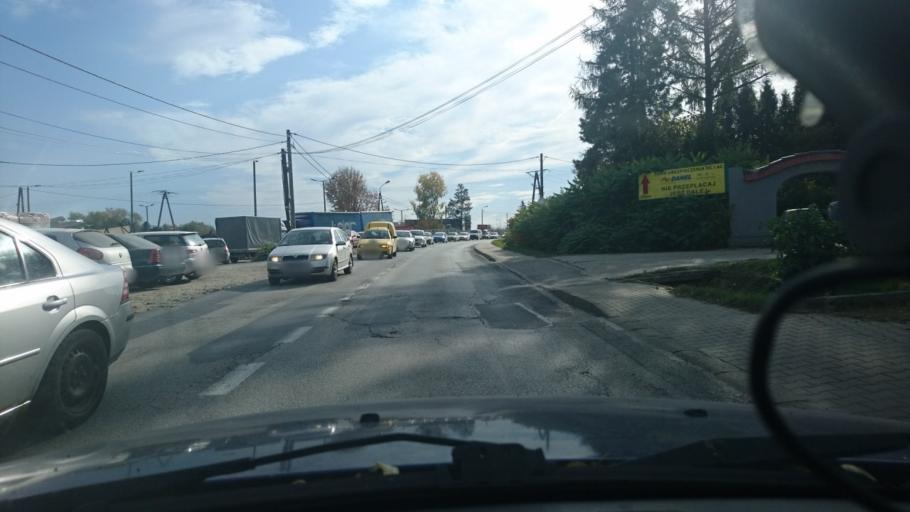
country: PL
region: Silesian Voivodeship
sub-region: Bielsko-Biala
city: Bielsko-Biala
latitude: 49.8539
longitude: 19.0356
